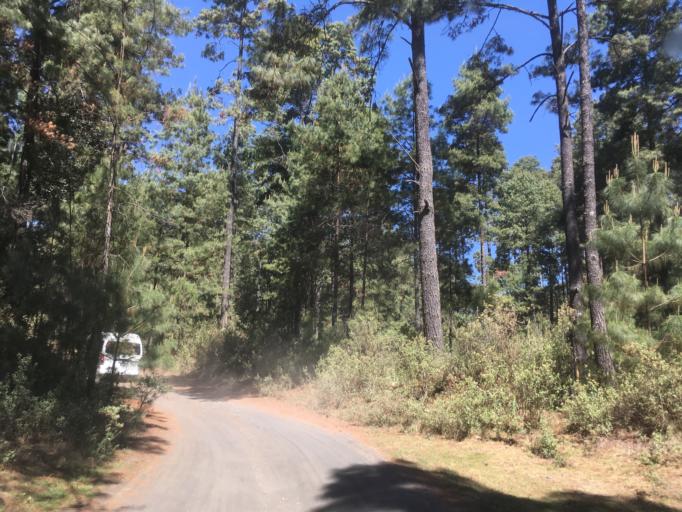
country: MX
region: Michoacan
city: Nuevo San Juan Parangaricutiro
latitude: 19.4587
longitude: -102.2056
